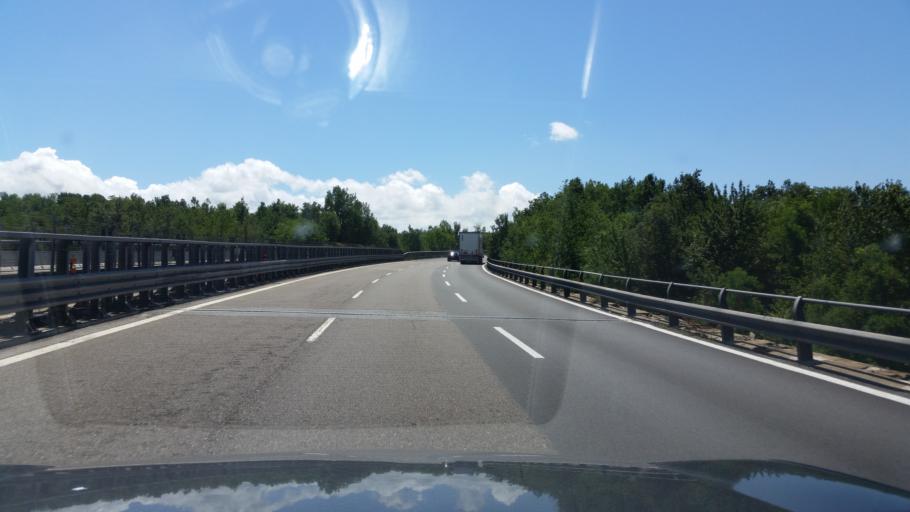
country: IT
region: Piedmont
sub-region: Provincia di Alessandria
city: Tagliolo Monferrato
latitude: 44.6500
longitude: 8.6616
